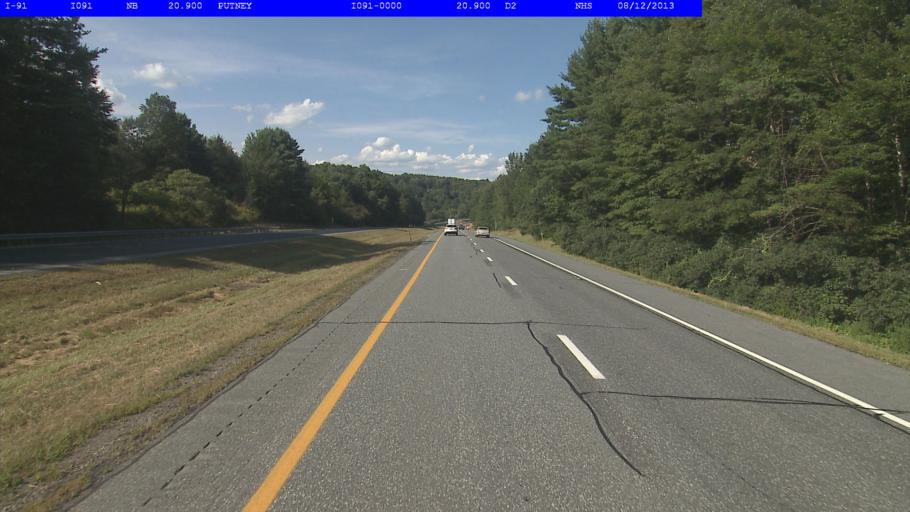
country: US
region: New Hampshire
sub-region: Cheshire County
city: Westmoreland
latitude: 42.9850
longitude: -72.4802
